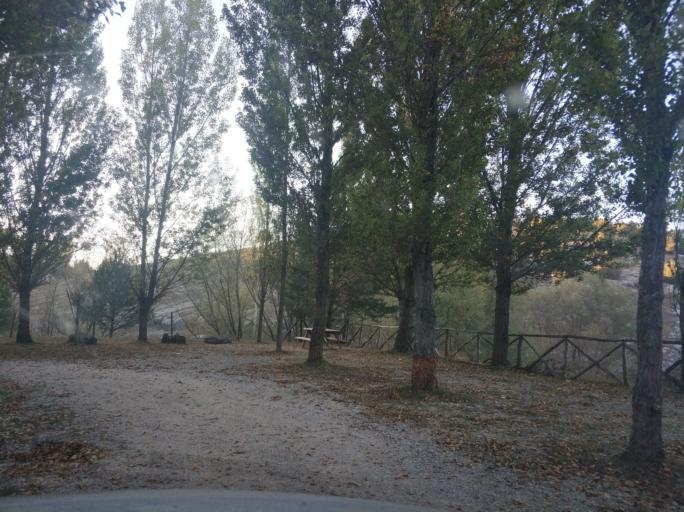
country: ES
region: Castille and Leon
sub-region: Provincia de Burgos
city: Hontoria del Pinar
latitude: 41.8413
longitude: -3.1591
